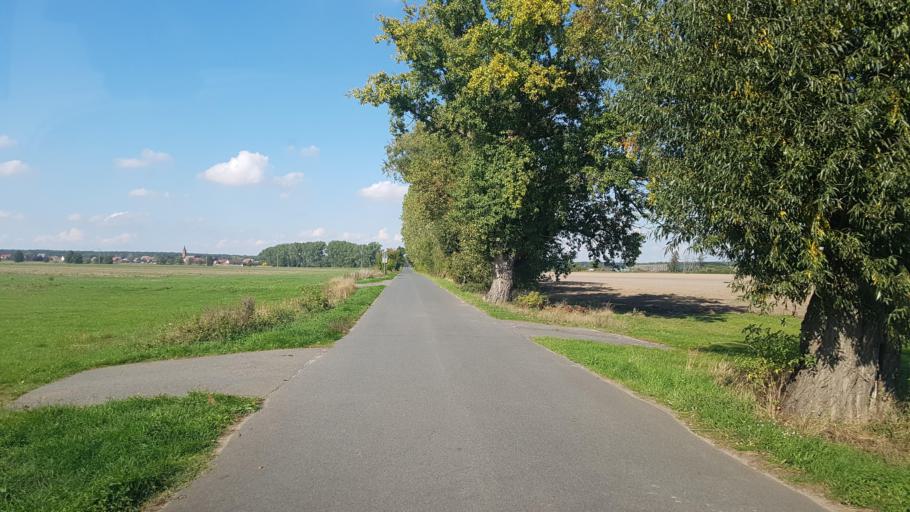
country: DE
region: Brandenburg
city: Ihlow
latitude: 51.8387
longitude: 13.2831
